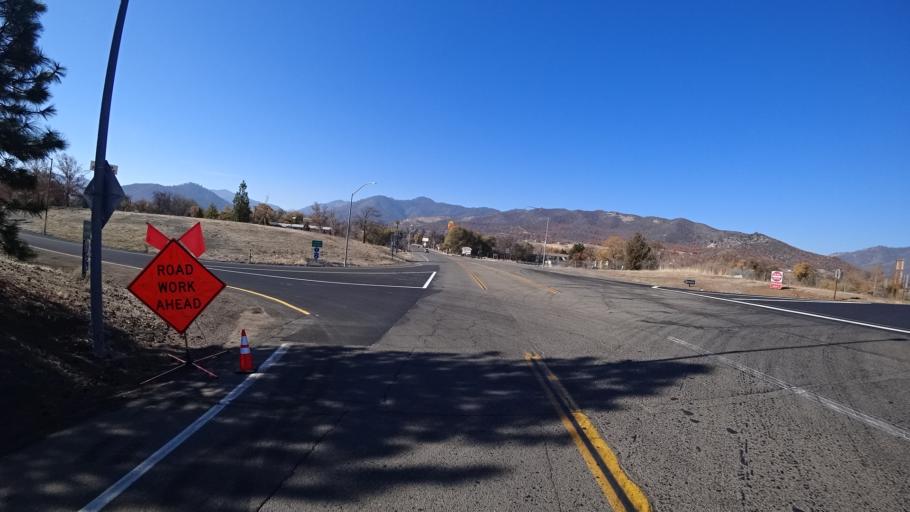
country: US
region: California
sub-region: Siskiyou County
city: Yreka
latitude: 41.7398
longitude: -122.6287
